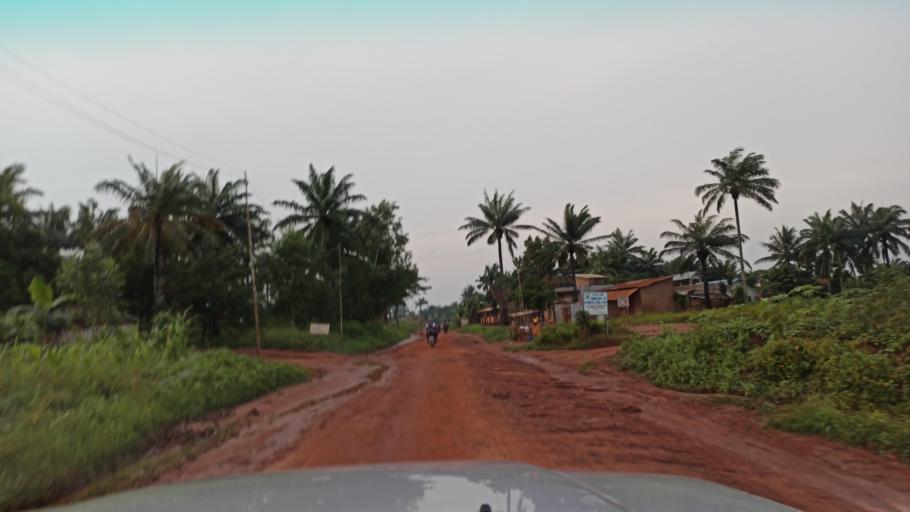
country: BJ
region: Queme
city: Porto-Novo
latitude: 6.5424
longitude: 2.6208
